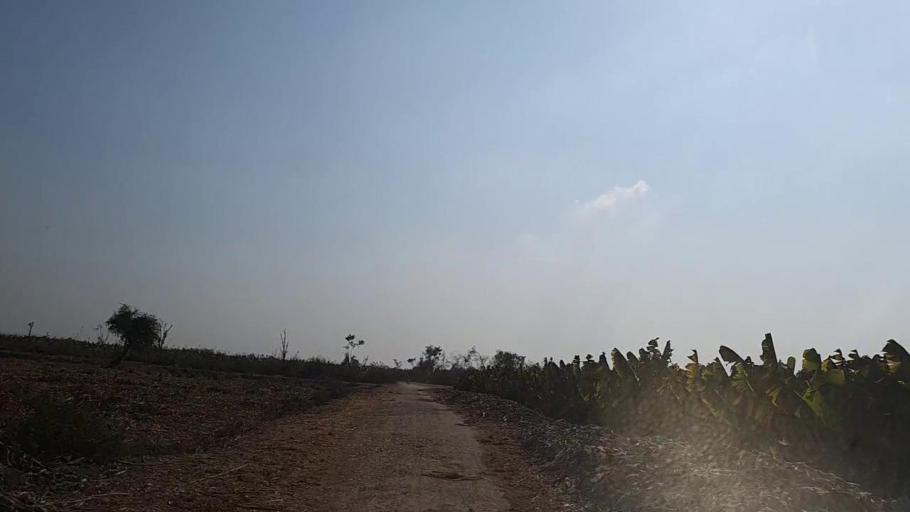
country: PK
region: Sindh
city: Daur
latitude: 26.4176
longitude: 68.2367
